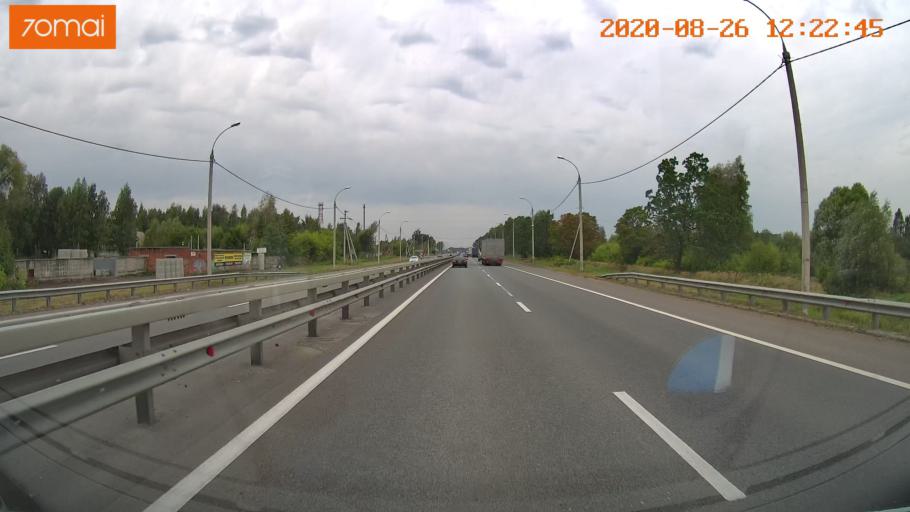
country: RU
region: Rjazan
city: Murmino
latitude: 54.5056
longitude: 39.9219
